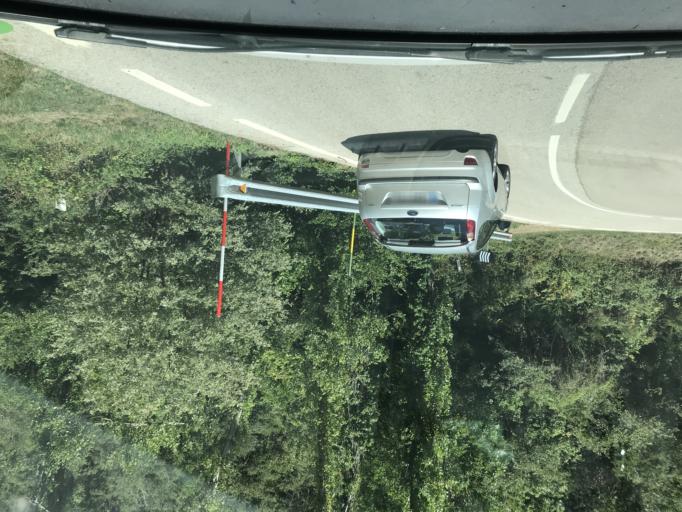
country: ES
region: Cantabria
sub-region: Provincia de Cantabria
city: Cabezon de Liebana
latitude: 43.0781
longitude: -4.4869
